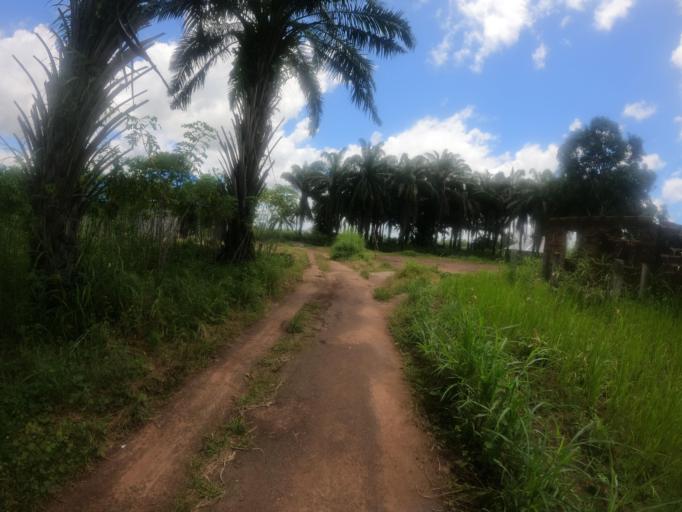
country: SL
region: Northern Province
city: Makeni
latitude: 8.8760
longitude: -12.0899
